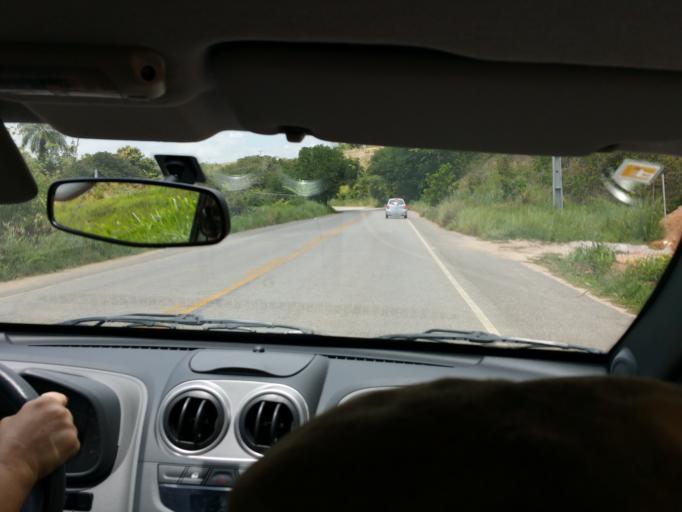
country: BR
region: Pernambuco
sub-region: Rio Formoso
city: Rio Formoso
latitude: -8.6909
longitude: -35.1367
